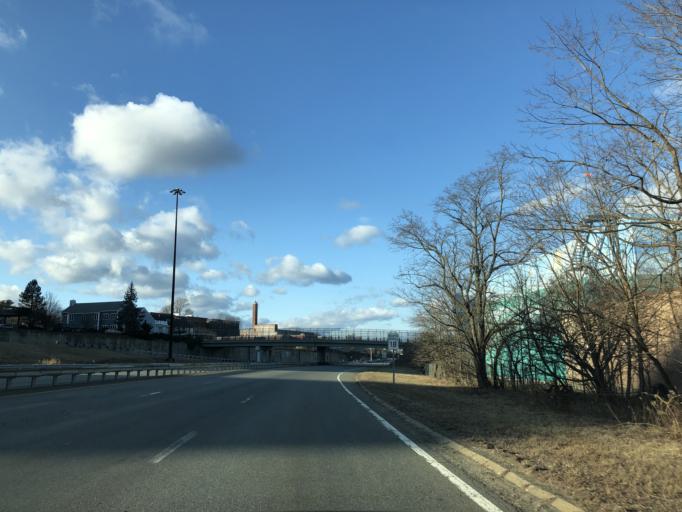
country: US
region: Massachusetts
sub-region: Bristol County
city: New Bedford
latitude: 41.6388
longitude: -70.9245
